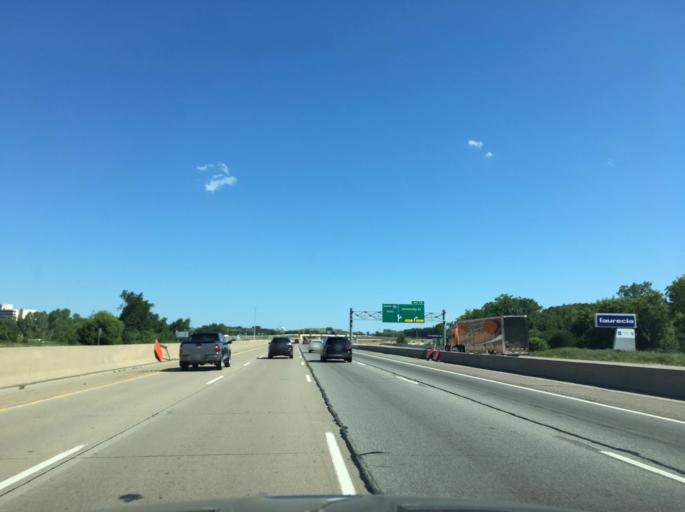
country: US
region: Michigan
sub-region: Oakland County
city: Auburn Hills
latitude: 42.6591
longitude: -83.2402
